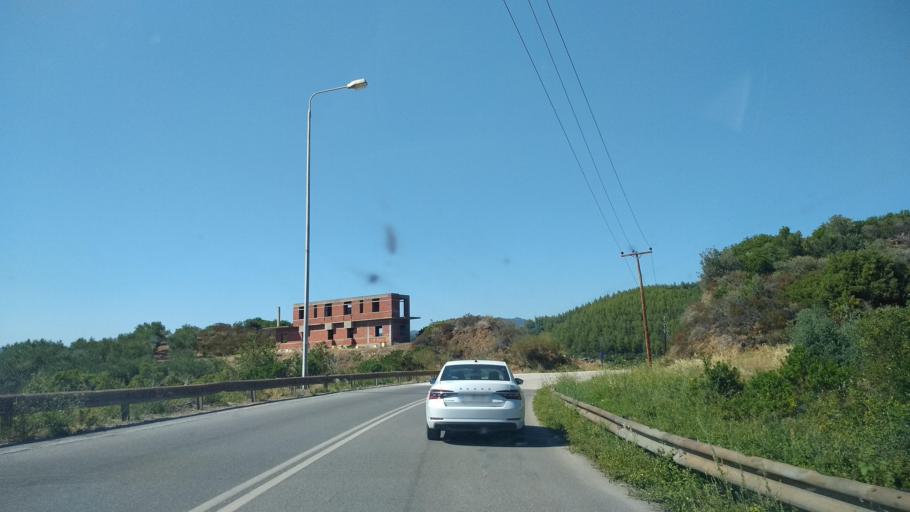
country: GR
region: Central Macedonia
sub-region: Nomos Chalkidikis
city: Sykia
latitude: 39.9763
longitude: 23.9110
